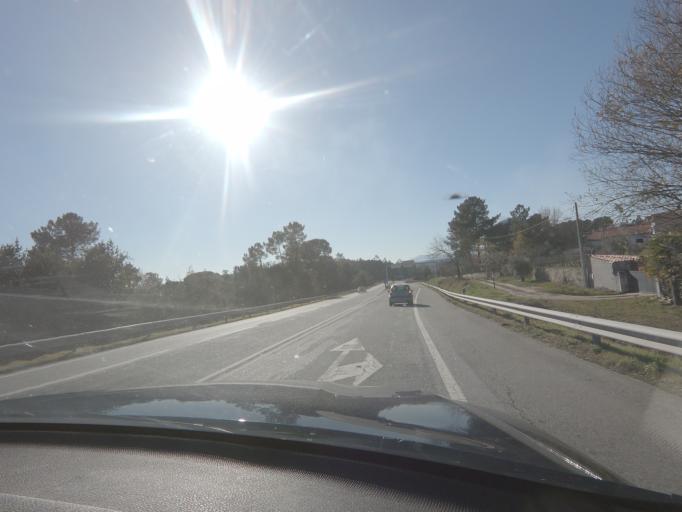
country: PT
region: Viseu
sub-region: Viseu
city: Abraveses
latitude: 40.6709
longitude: -7.9874
